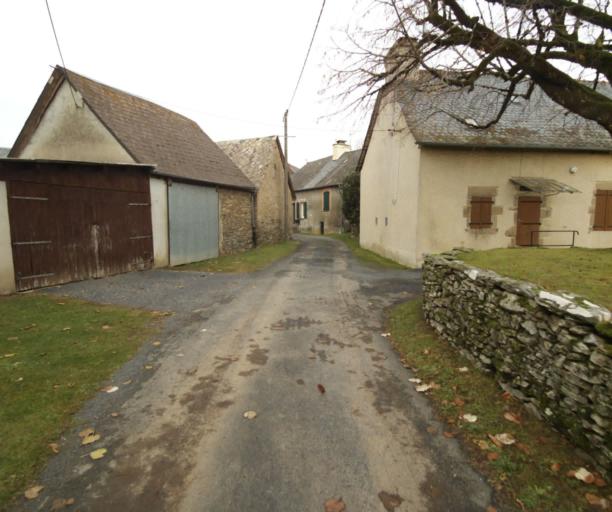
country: FR
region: Limousin
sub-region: Departement de la Correze
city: Sainte-Fortunade
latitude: 45.1750
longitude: 1.7687
